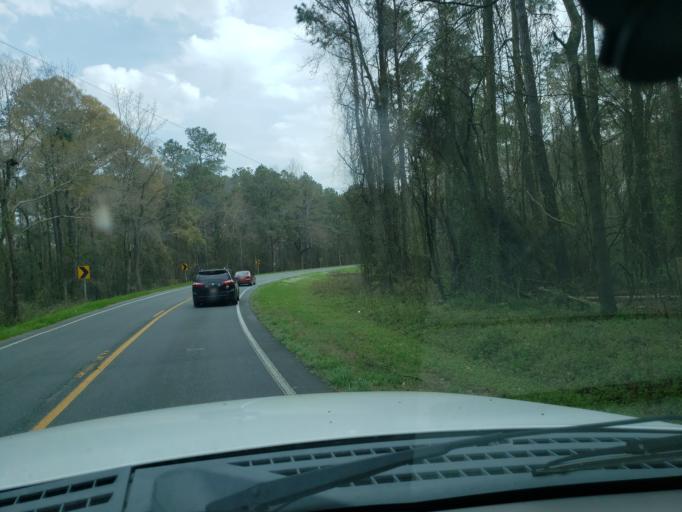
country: US
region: North Carolina
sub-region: Duplin County
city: Beulaville
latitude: 34.7886
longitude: -77.8398
